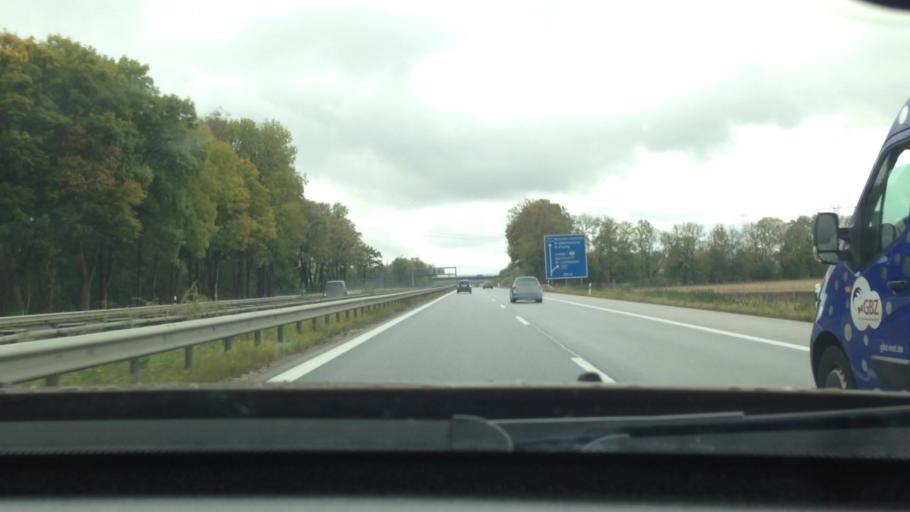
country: DE
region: Bavaria
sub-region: Upper Bavaria
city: Karlsfeld
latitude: 48.1887
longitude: 11.4212
